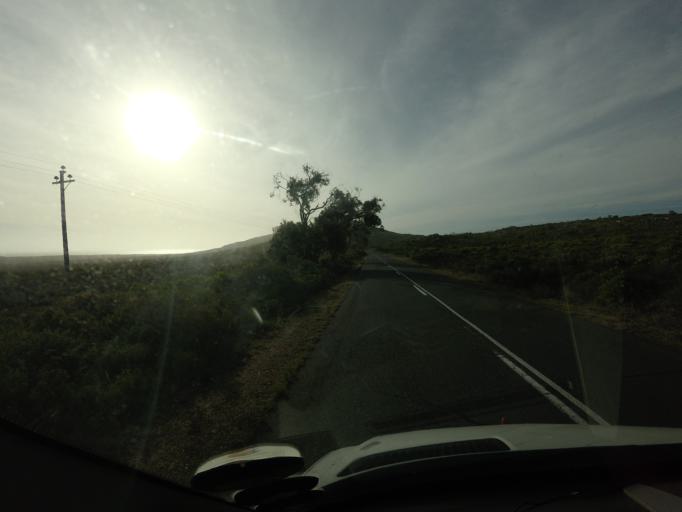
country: ZA
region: Western Cape
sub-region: City of Cape Town
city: Retreat
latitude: -34.2314
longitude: 18.4138
